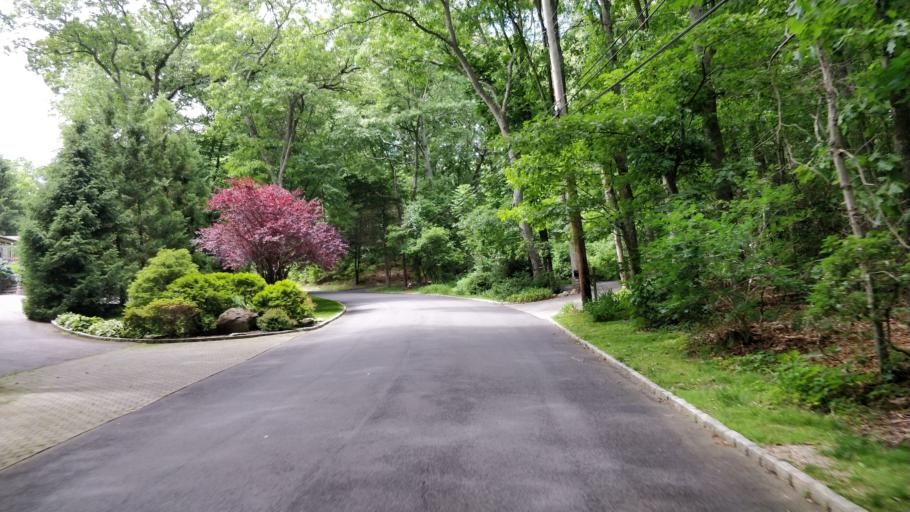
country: US
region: New York
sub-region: Nassau County
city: Laurel Hollow
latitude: 40.8433
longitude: -73.4655
